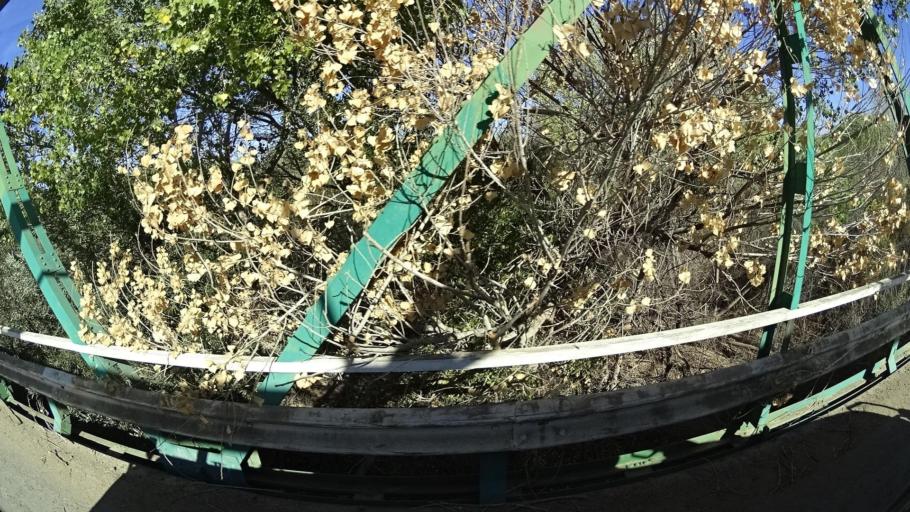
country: US
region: California
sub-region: Monterey County
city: King City
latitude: 36.1170
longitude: -121.0279
